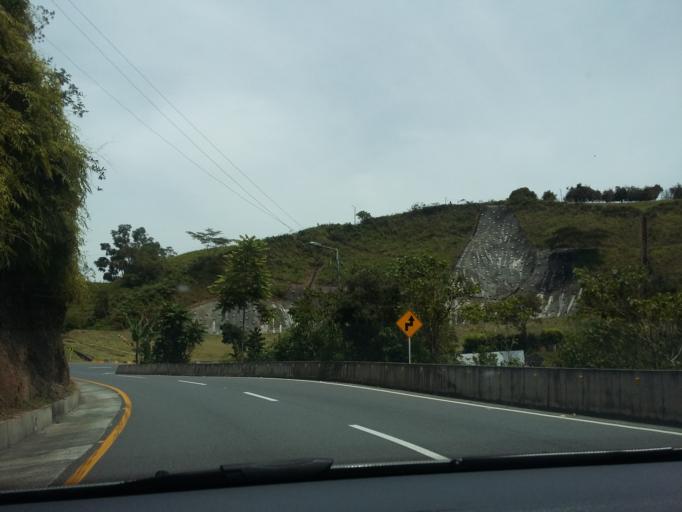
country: CO
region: Santander
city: Bucaramanga
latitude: 7.1141
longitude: -73.0789
